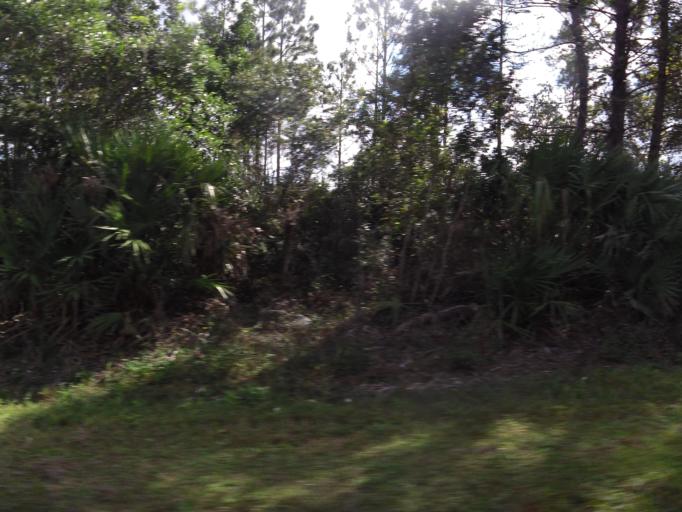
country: US
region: Florida
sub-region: Saint Johns County
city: Villano Beach
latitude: 30.0115
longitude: -81.3963
